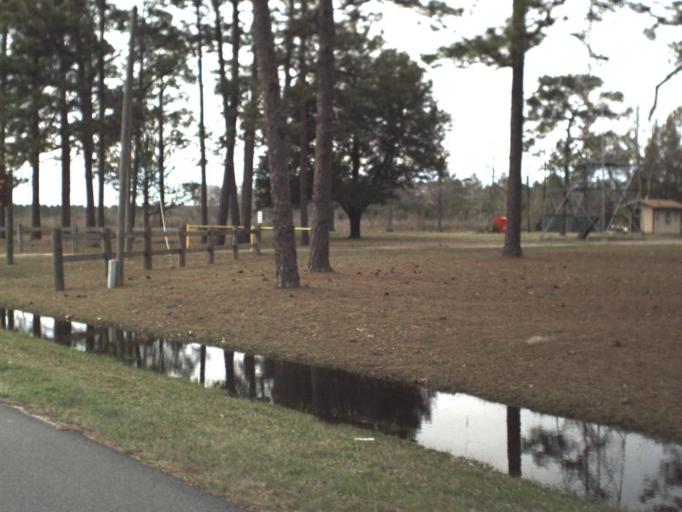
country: US
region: Florida
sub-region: Gulf County
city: Wewahitchka
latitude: 30.1412
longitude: -85.2713
